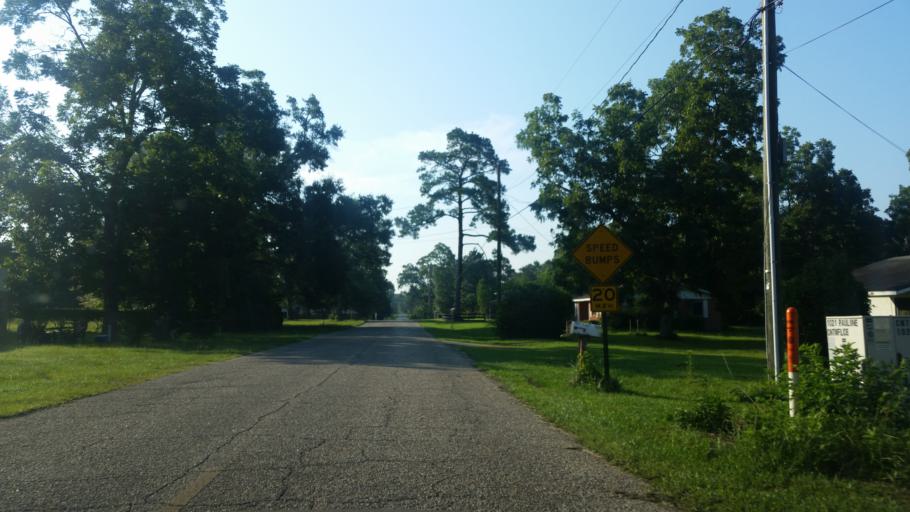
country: US
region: Florida
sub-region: Escambia County
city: Gonzalez
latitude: 30.5901
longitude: -87.3031
